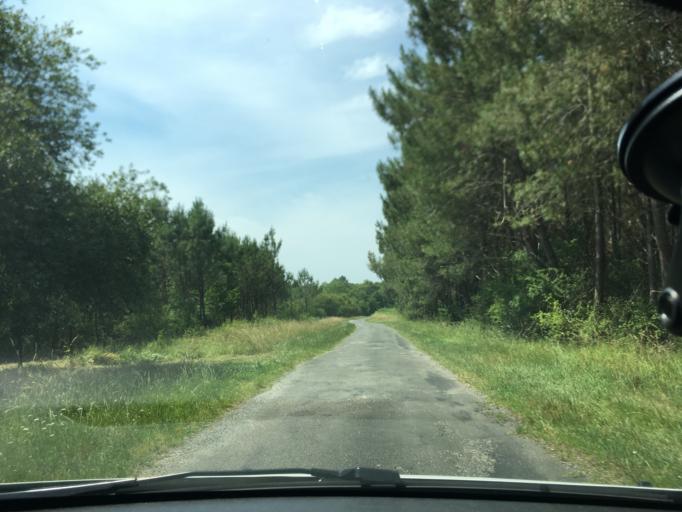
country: FR
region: Aquitaine
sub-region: Departement de la Gironde
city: Lesparre-Medoc
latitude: 45.2837
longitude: -0.9014
